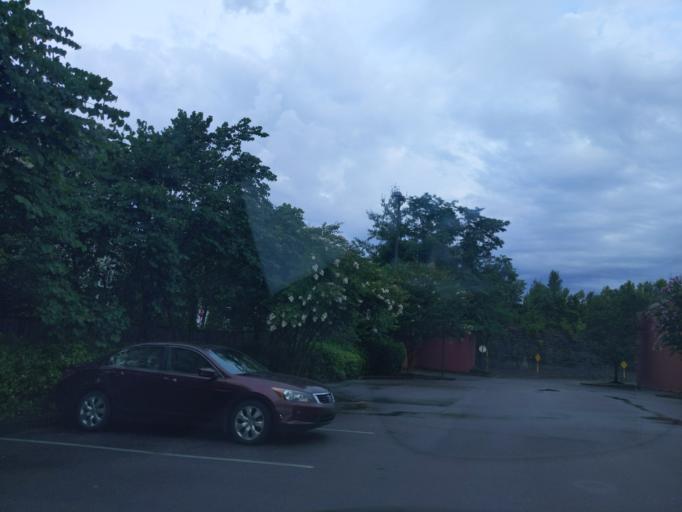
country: US
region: Tennessee
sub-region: Williamson County
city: Brentwood Estates
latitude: 36.0387
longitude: -86.7451
